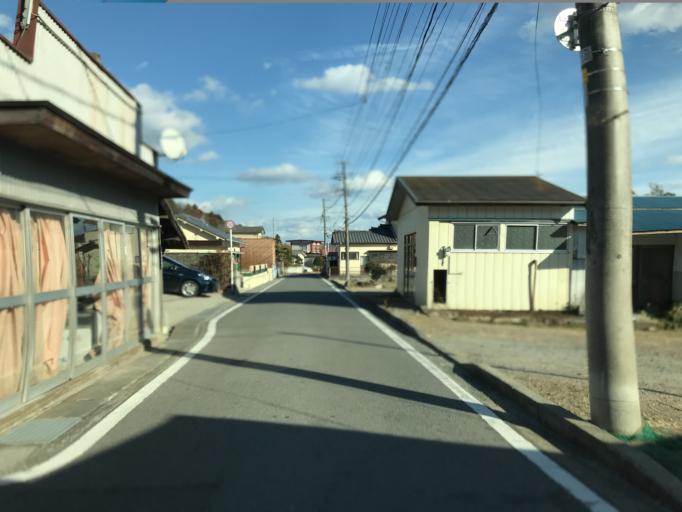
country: JP
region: Fukushima
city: Iwaki
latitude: 37.1269
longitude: 140.8455
